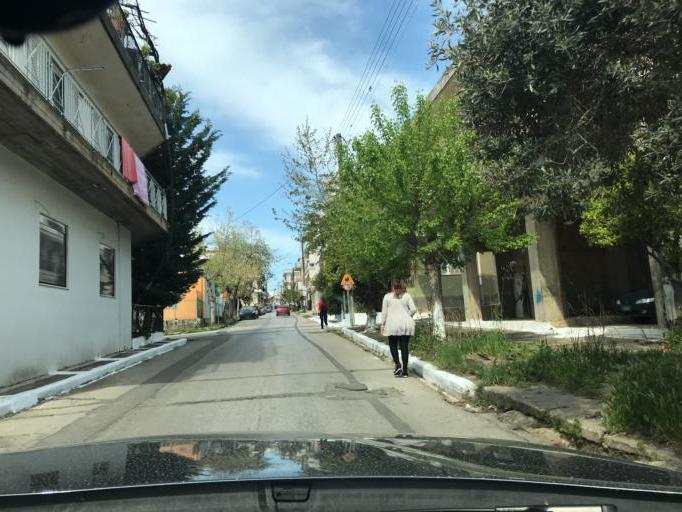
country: GR
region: West Greece
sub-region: Nomos Ileias
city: Pyrgos
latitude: 37.6719
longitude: 21.4485
